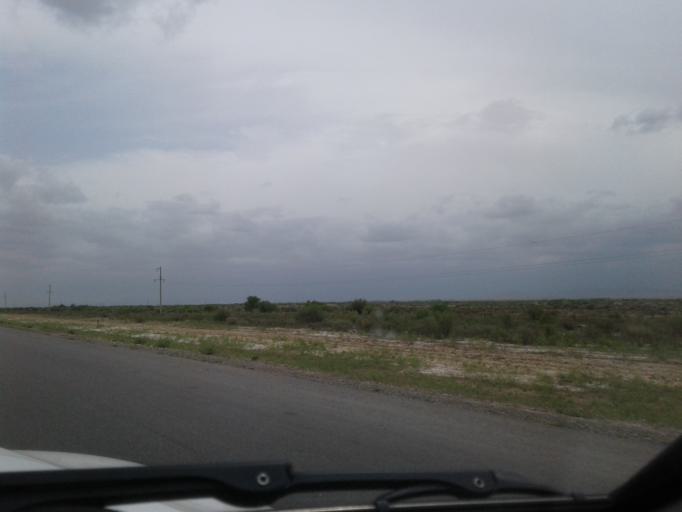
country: TM
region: Ahal
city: Kaka
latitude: 37.5030
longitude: 59.4517
